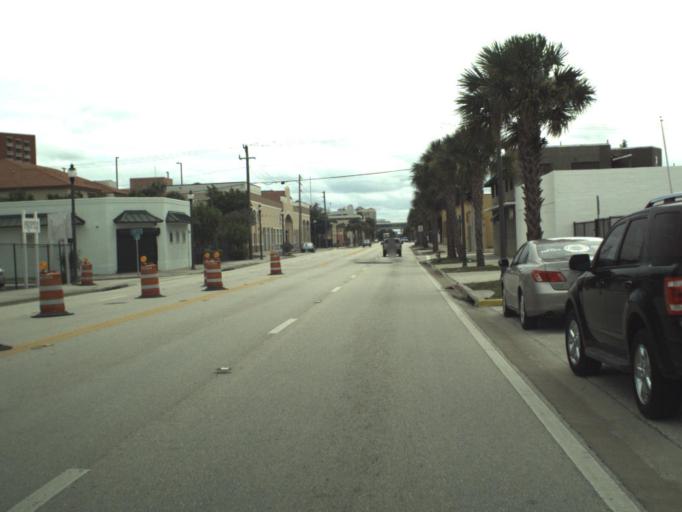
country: US
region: Florida
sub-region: Palm Beach County
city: West Palm Beach
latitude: 26.7307
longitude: -80.0531
